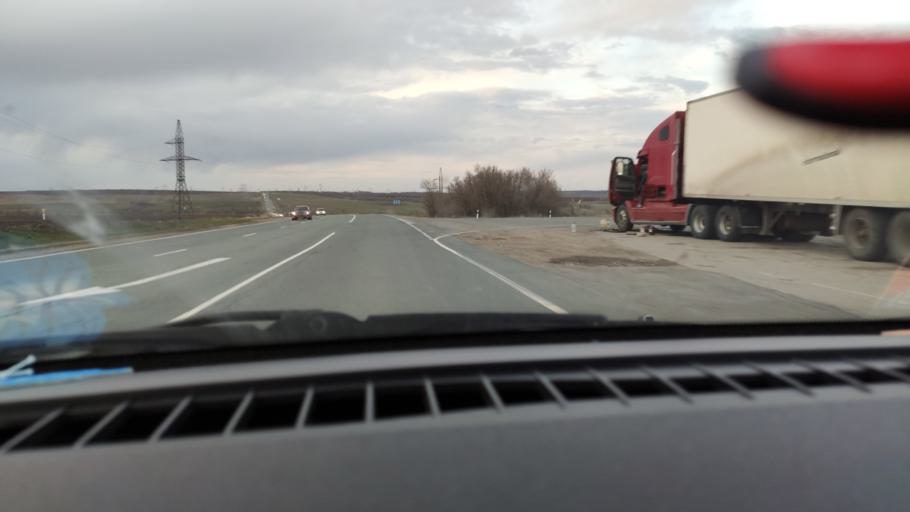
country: RU
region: Saratov
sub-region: Saratovskiy Rayon
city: Saratov
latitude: 51.7511
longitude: 46.0605
